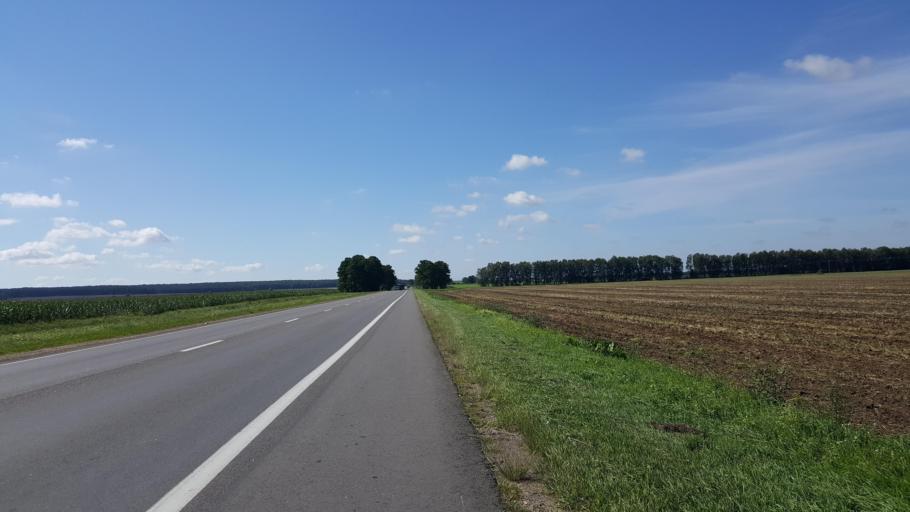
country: BY
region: Brest
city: Kamyanyets
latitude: 52.3199
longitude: 23.7820
